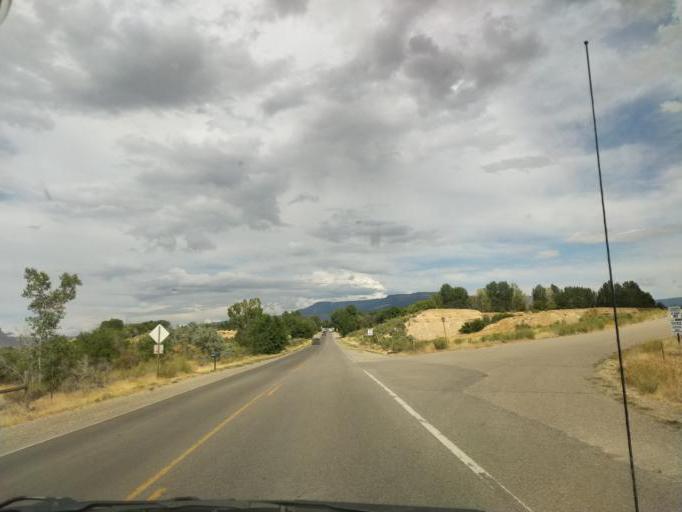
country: US
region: Colorado
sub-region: Mesa County
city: Clifton
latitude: 39.0549
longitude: -108.4567
